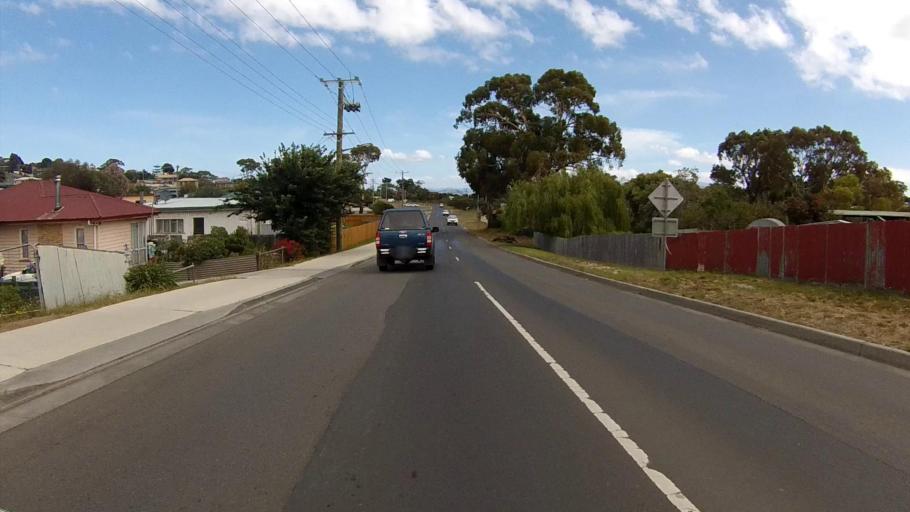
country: AU
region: Tasmania
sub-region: Sorell
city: Sorell
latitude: -42.8580
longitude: 147.6164
